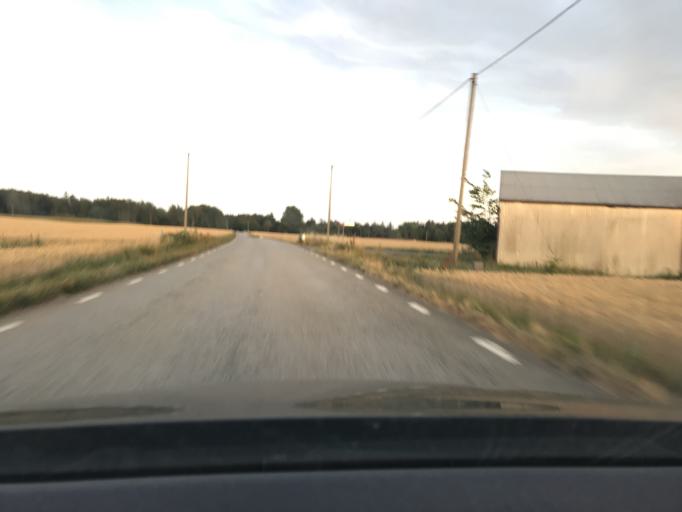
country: SE
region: Skane
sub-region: Simrishamns Kommun
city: Simrishamn
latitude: 55.4388
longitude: 14.2249
